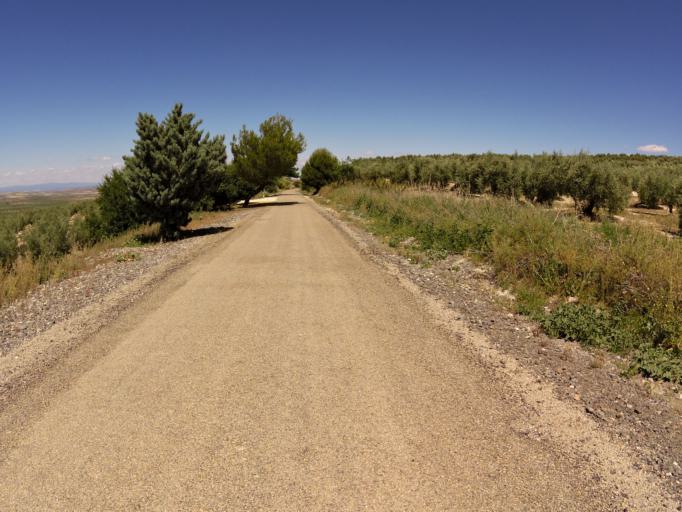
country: ES
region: Andalusia
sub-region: Provincia de Jaen
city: Torre del Campo
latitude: 37.7906
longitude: -3.8777
